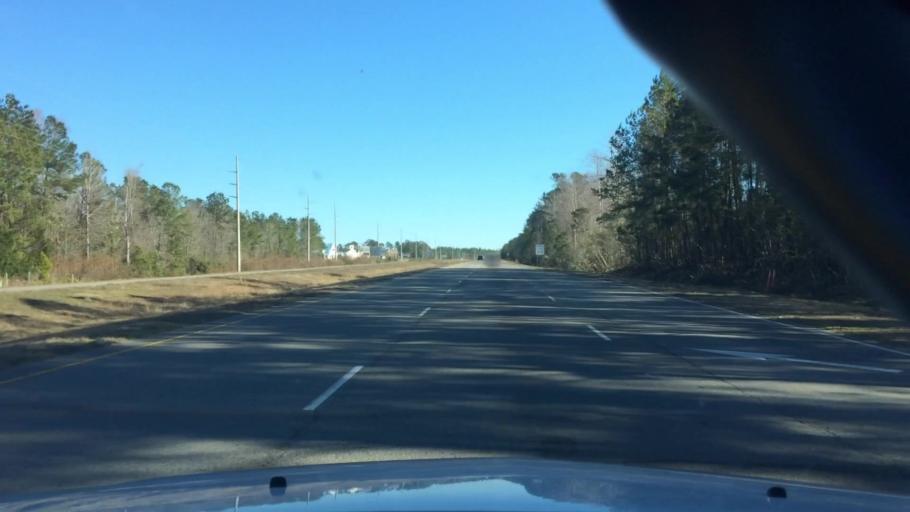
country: US
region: North Carolina
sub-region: Brunswick County
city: Shallotte
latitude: 33.9803
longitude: -78.3995
